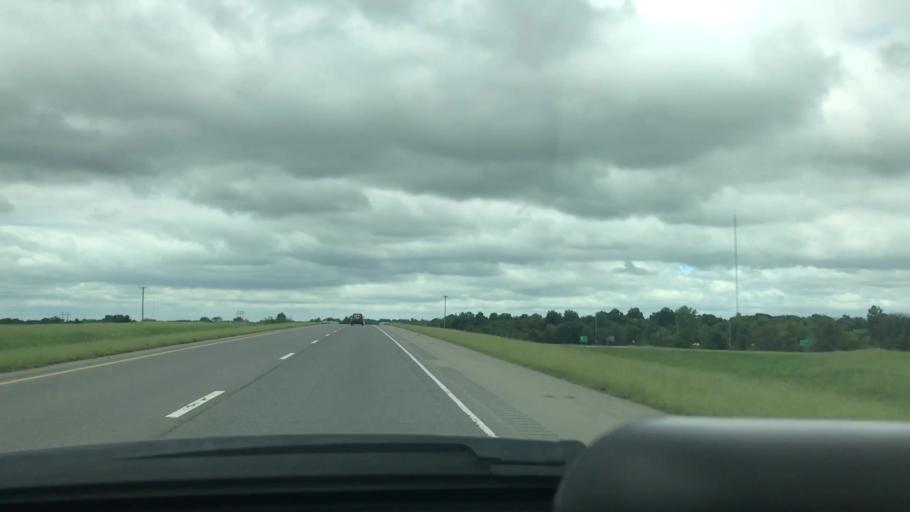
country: US
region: Oklahoma
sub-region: McIntosh County
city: Checotah
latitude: 35.5742
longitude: -95.4909
